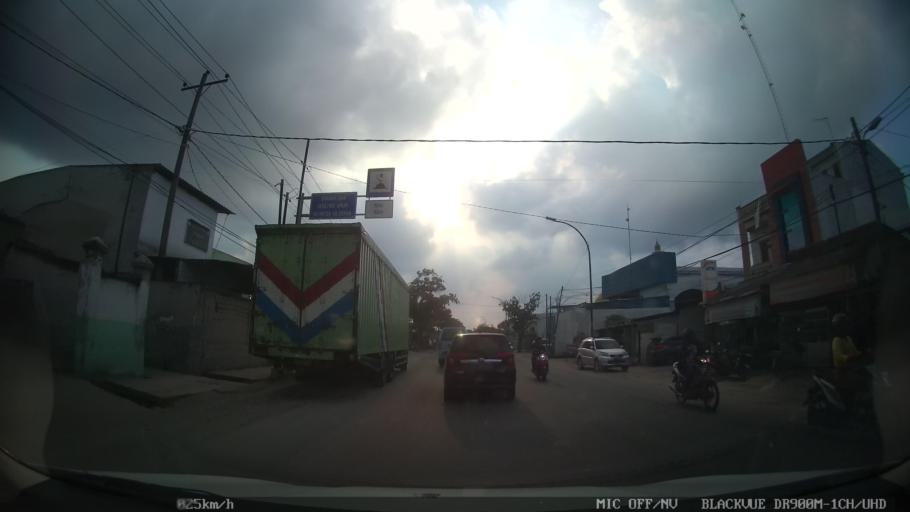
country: ID
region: North Sumatra
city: Medan
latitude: 3.5972
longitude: 98.7319
